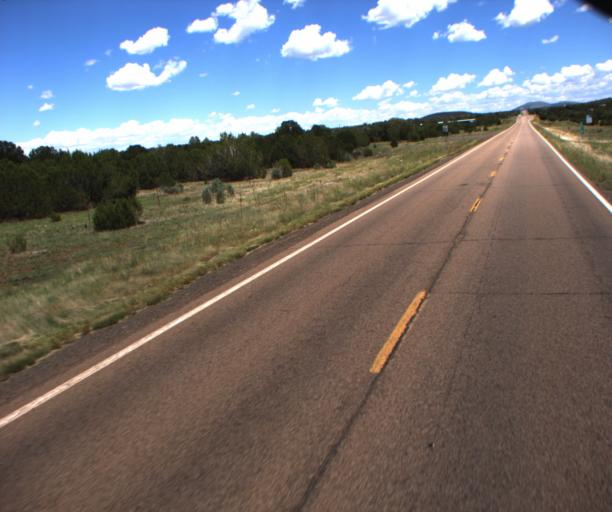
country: US
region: Arizona
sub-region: Navajo County
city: Pinetop-Lakeside
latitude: 34.2761
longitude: -109.7854
